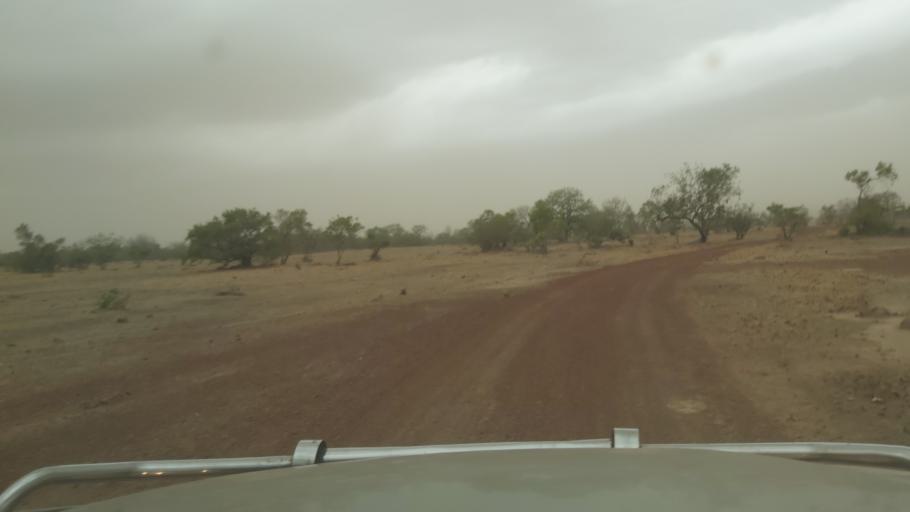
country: ML
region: Koulikoro
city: Banamba
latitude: 13.3642
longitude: -7.1793
